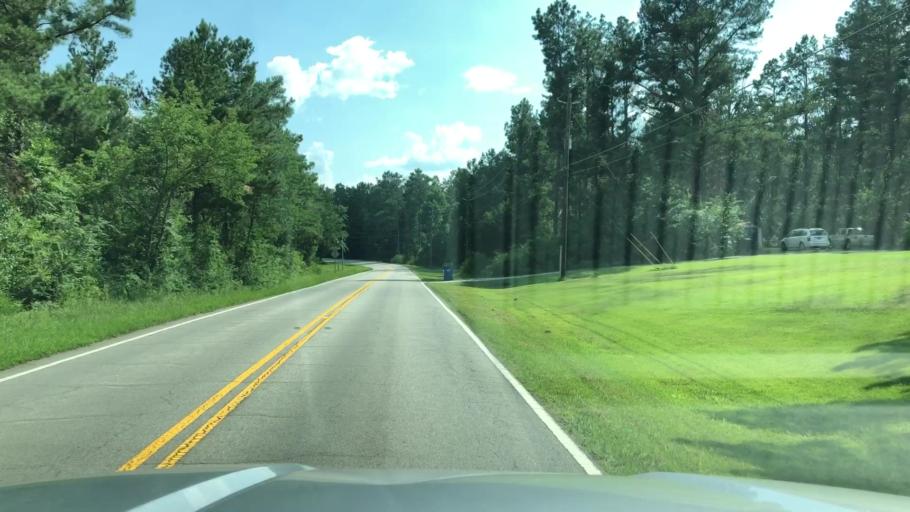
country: US
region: Georgia
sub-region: Paulding County
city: Dallas
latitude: 33.9546
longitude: -84.8408
